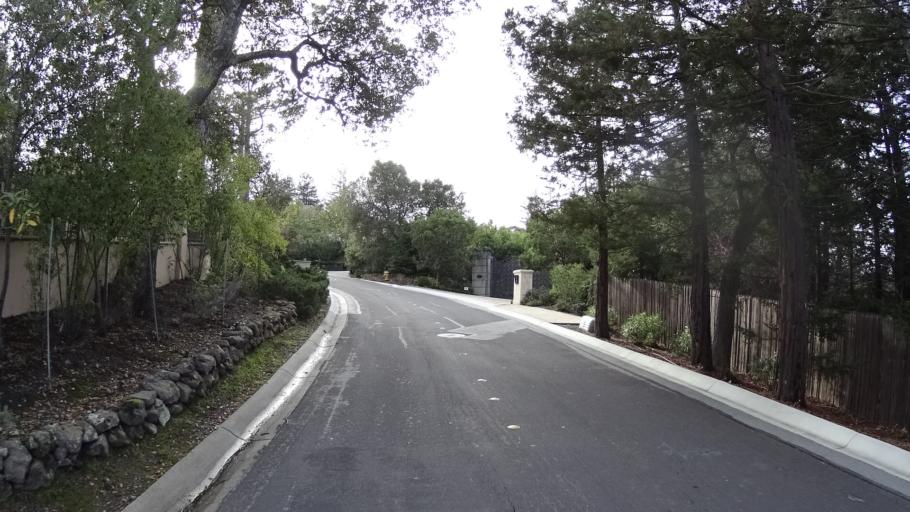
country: US
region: California
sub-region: San Mateo County
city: Hillsborough
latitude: 37.5617
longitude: -122.3668
